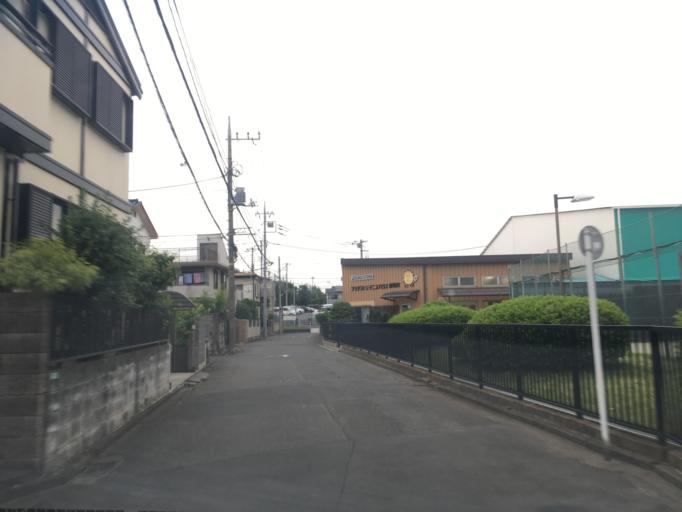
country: JP
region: Saitama
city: Tokorozawa
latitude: 35.8082
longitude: 139.4474
